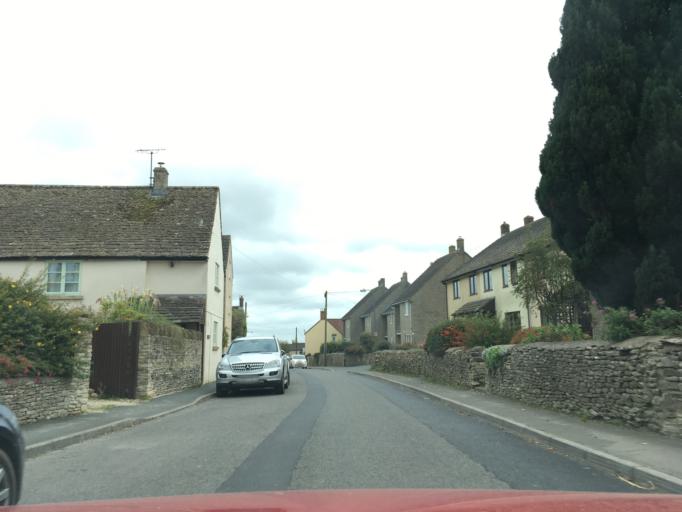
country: GB
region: England
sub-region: South Gloucestershire
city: Horton
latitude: 51.5813
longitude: -2.3215
